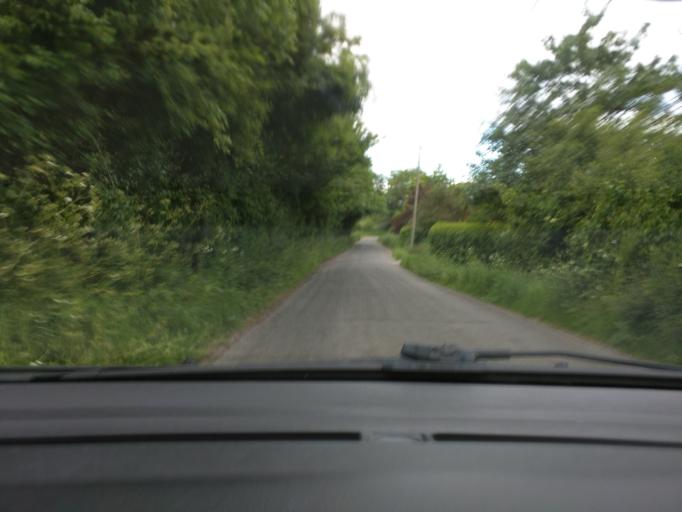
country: GB
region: England
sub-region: Suffolk
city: Saxmundham
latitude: 52.2298
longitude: 1.4759
